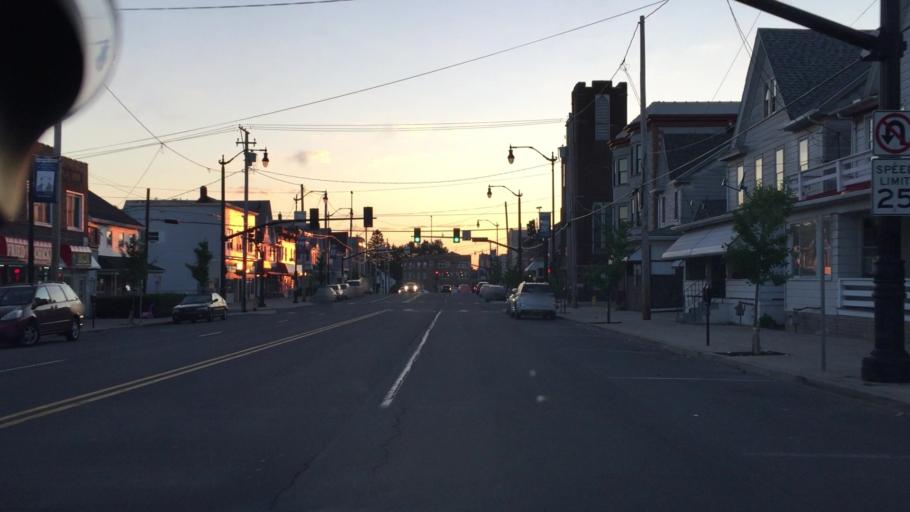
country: US
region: Pennsylvania
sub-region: Luzerne County
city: West Hazleton
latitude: 40.9586
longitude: -75.9931
